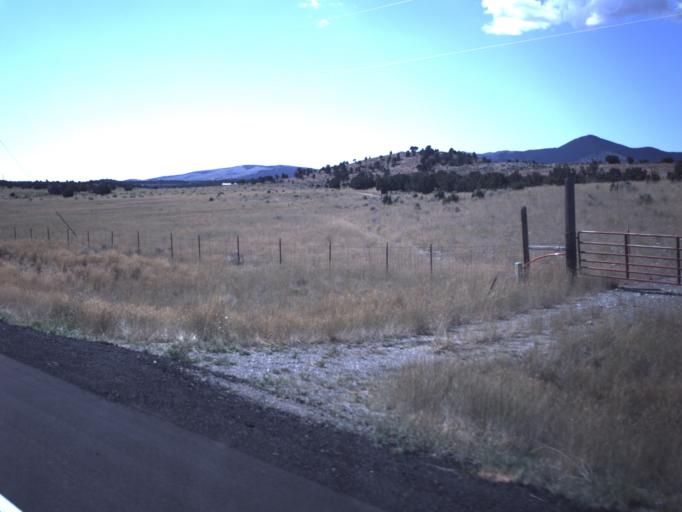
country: US
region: Utah
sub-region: Utah County
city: Eagle Mountain
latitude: 40.0415
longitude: -112.2905
